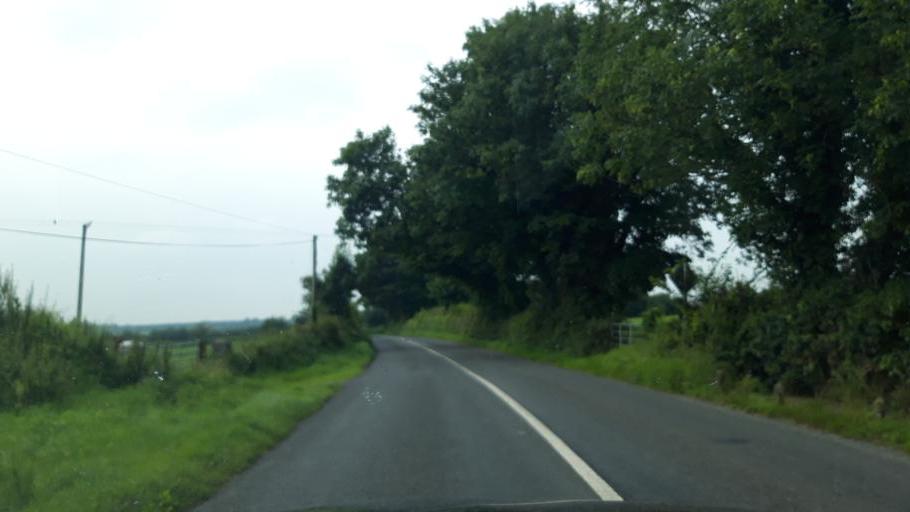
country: IE
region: Munster
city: Fethard
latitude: 52.5866
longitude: -7.5943
